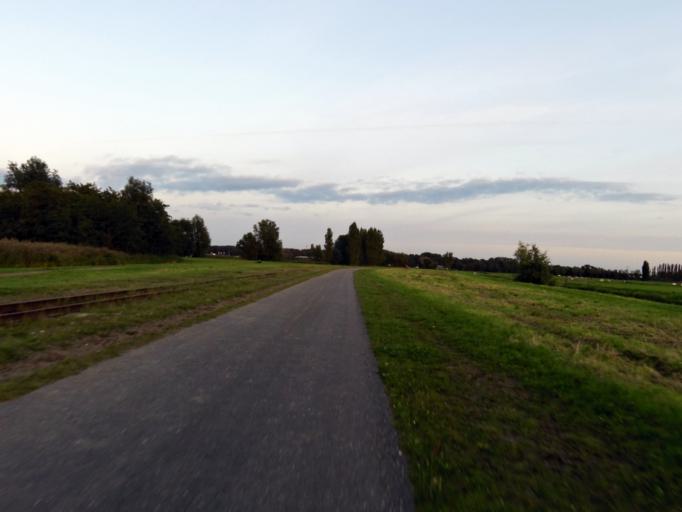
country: NL
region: South Holland
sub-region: Gemeente Wassenaar
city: Wassenaar
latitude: 52.1585
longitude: 4.4318
